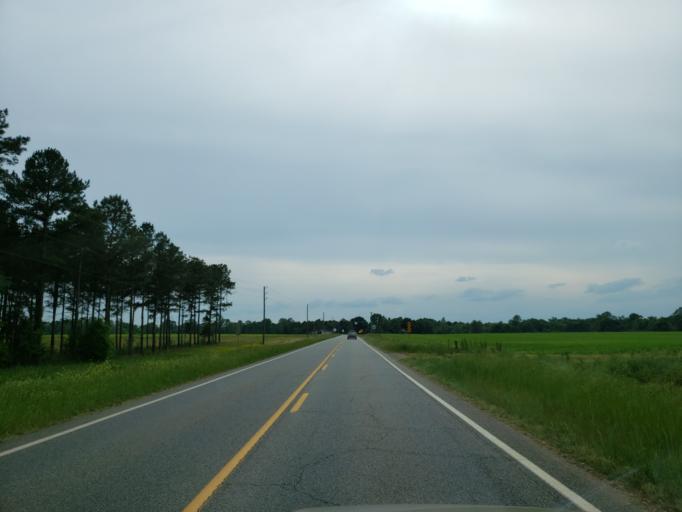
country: US
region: Georgia
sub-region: Macon County
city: Marshallville
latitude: 32.3680
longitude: -83.9001
